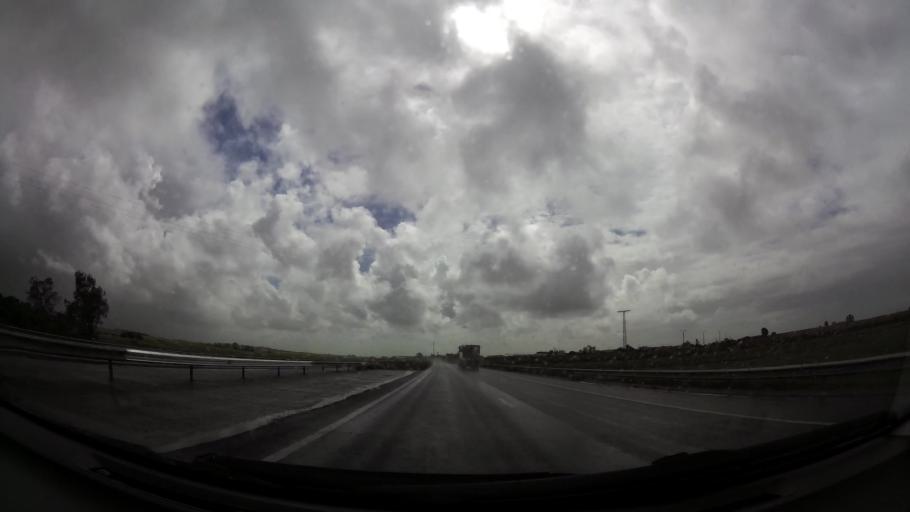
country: MA
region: Grand Casablanca
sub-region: Nouaceur
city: Dar Bouazza
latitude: 33.3872
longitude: -7.8843
